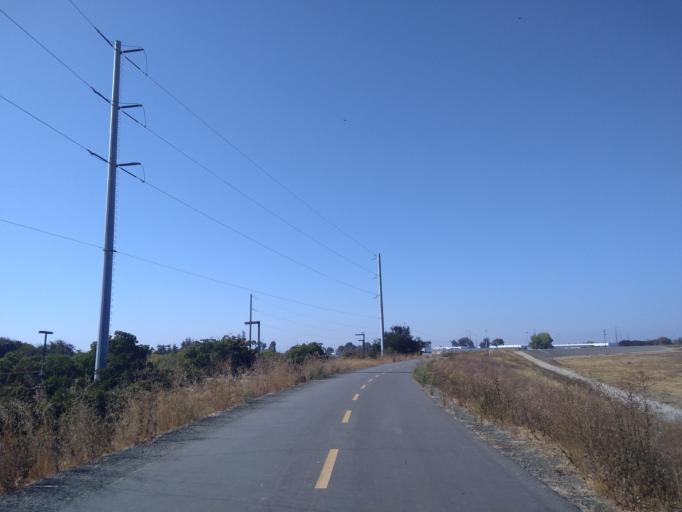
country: US
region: California
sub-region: Santa Clara County
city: Milpitas
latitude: 37.4148
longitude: -121.9292
